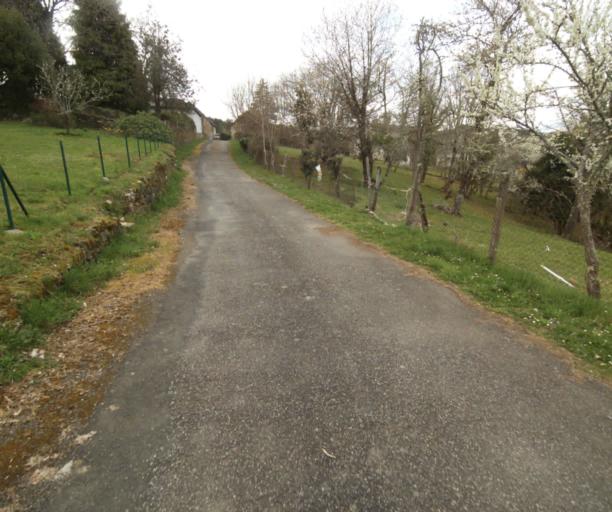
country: FR
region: Limousin
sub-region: Departement de la Correze
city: Argentat
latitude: 45.1964
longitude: 1.9722
